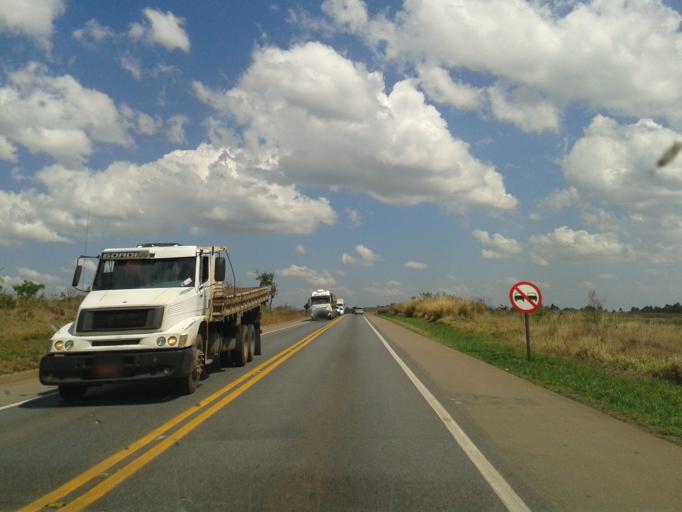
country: BR
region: Minas Gerais
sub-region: Campos Altos
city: Campos Altos
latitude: -19.6861
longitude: -46.0391
